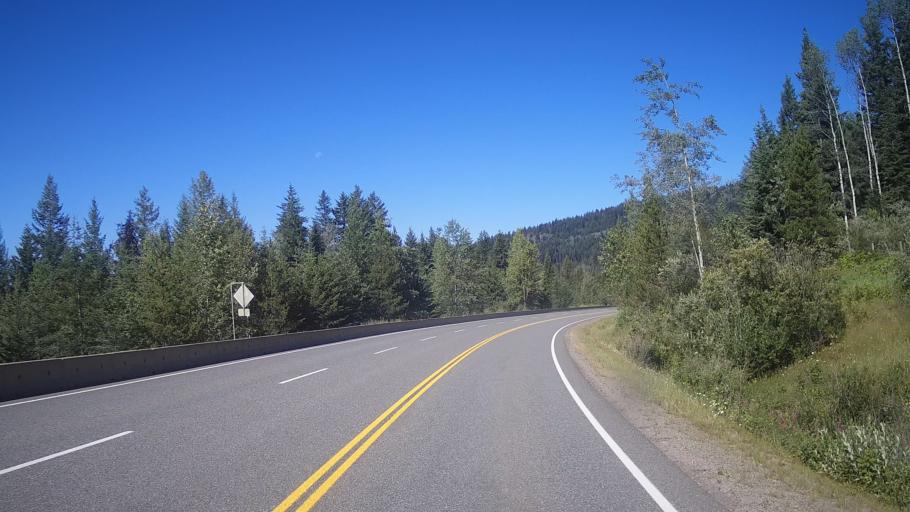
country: CA
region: British Columbia
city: Kamloops
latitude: 51.4762
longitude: -120.4774
